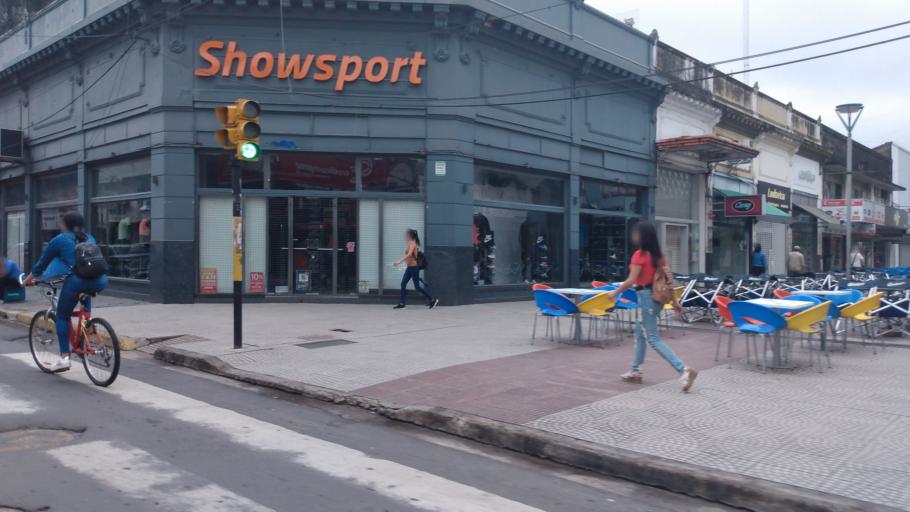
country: AR
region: Corrientes
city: Corrientes
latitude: -27.4680
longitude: -58.8331
